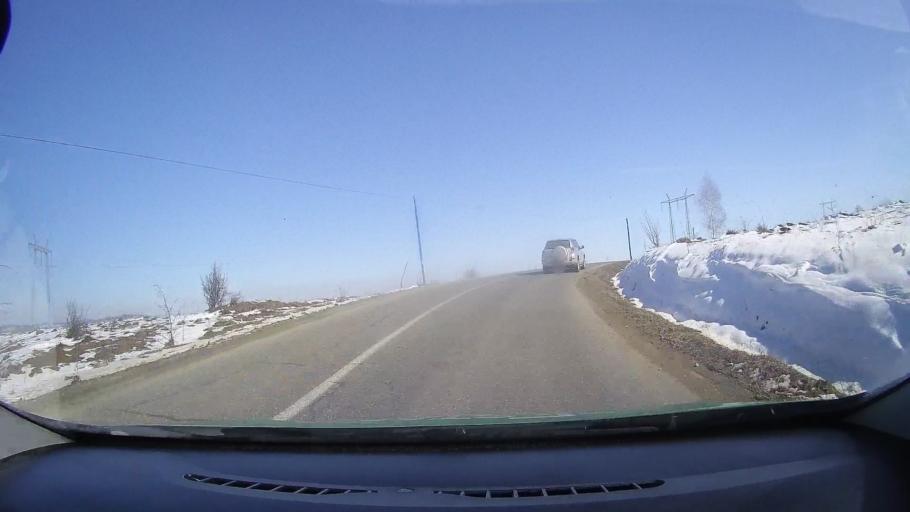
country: RO
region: Brasov
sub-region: Oras Victoria
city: Victoria
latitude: 45.7330
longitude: 24.7233
